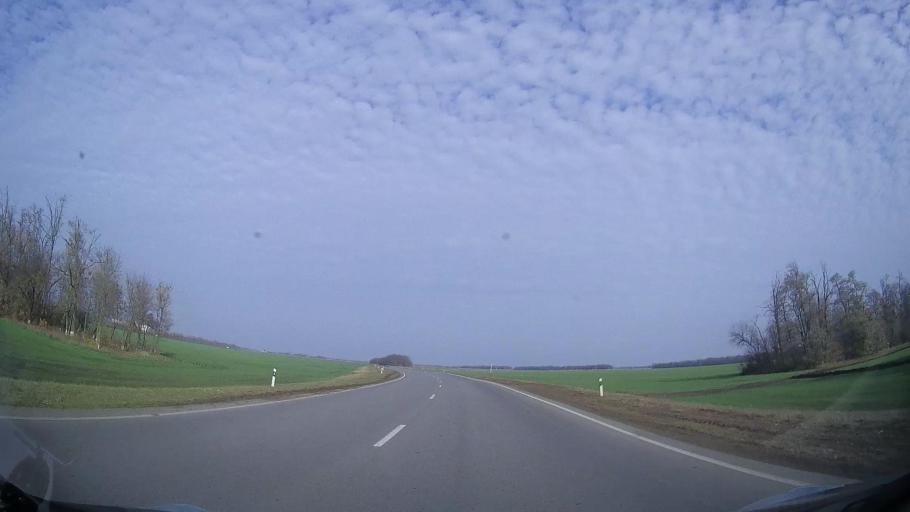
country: RU
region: Rostov
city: Tselina
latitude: 46.5168
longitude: 41.0721
